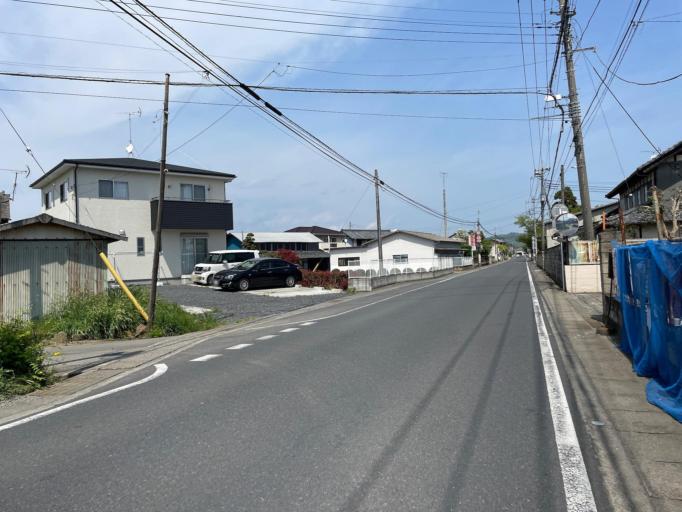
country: JP
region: Gunma
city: Ota
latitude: 36.2882
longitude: 139.3385
